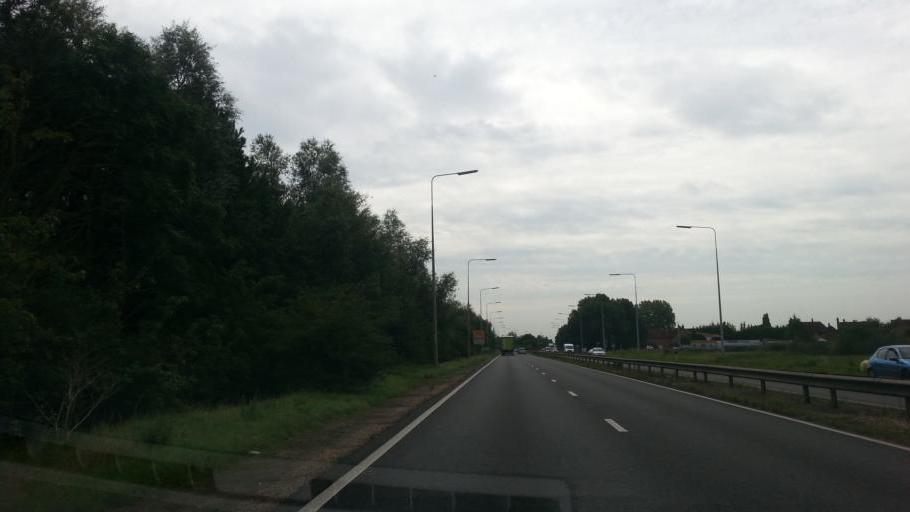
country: GB
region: England
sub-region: Central Bedfordshire
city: Sandy
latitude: 52.1080
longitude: -0.2814
